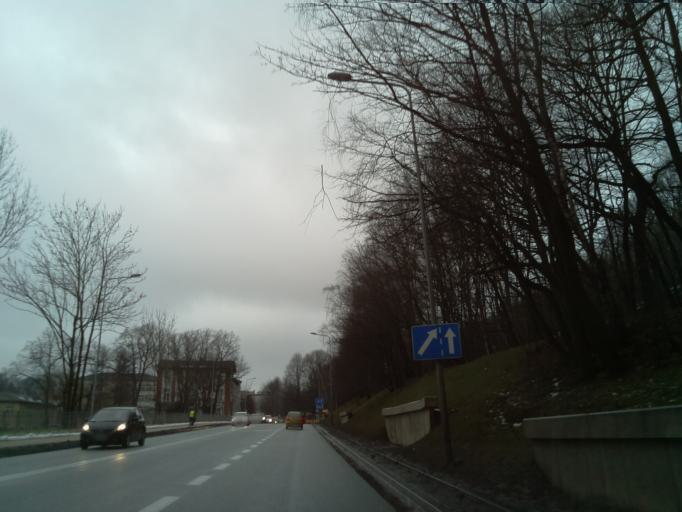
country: PL
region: Lower Silesian Voivodeship
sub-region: Powiat walbrzyski
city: Walbrzych
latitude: 50.7944
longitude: 16.2878
